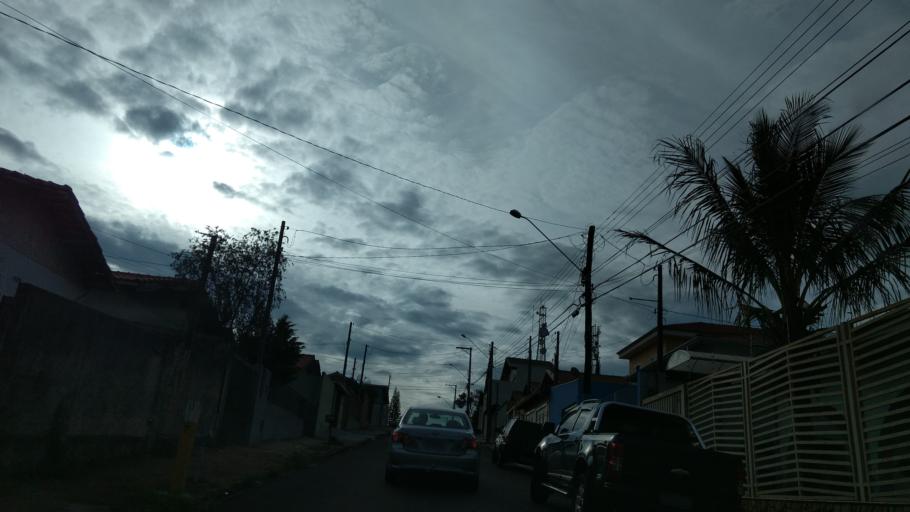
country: BR
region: Sao Paulo
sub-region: Botucatu
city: Botucatu
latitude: -22.9006
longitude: -48.4448
